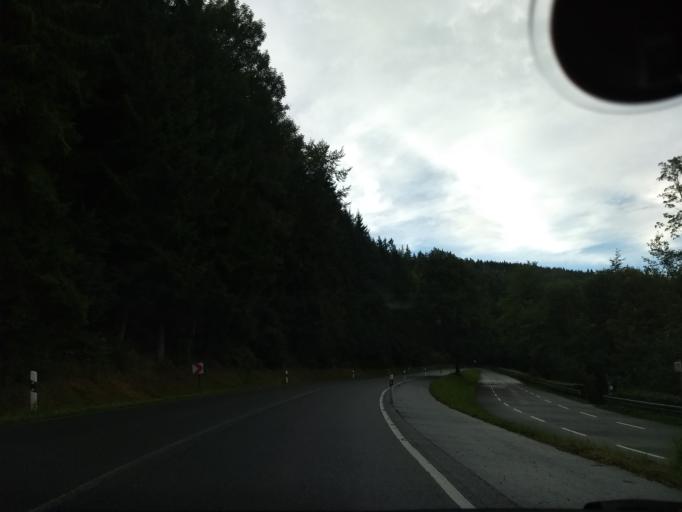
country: DE
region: North Rhine-Westphalia
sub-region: Regierungsbezirk Arnsberg
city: Meschede
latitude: 51.3228
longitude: 8.2577
